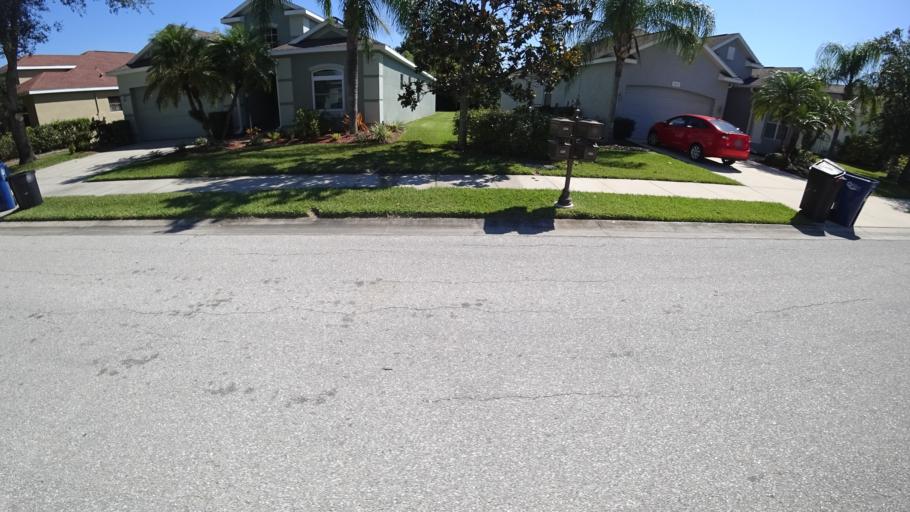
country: US
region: Florida
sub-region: Manatee County
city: Ellenton
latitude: 27.5623
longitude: -82.4426
